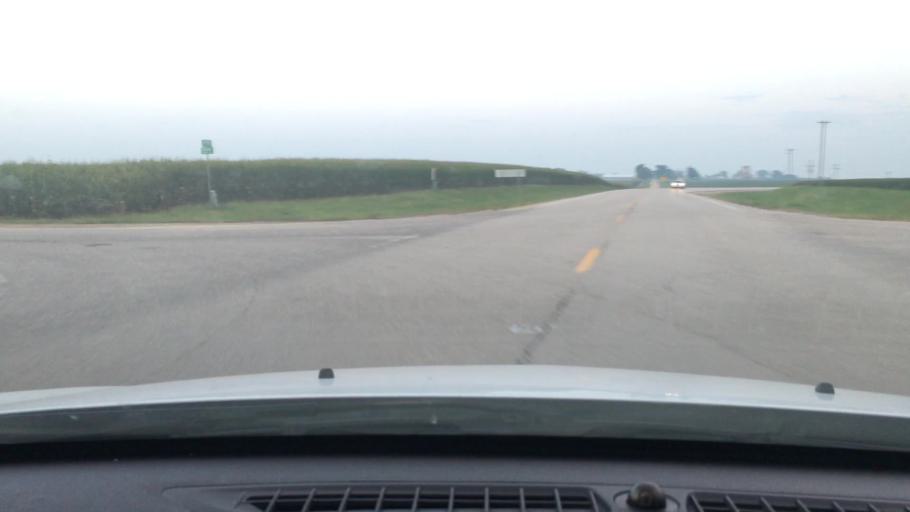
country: US
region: Illinois
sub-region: Ogle County
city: Rochelle
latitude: 41.8470
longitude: -89.0734
